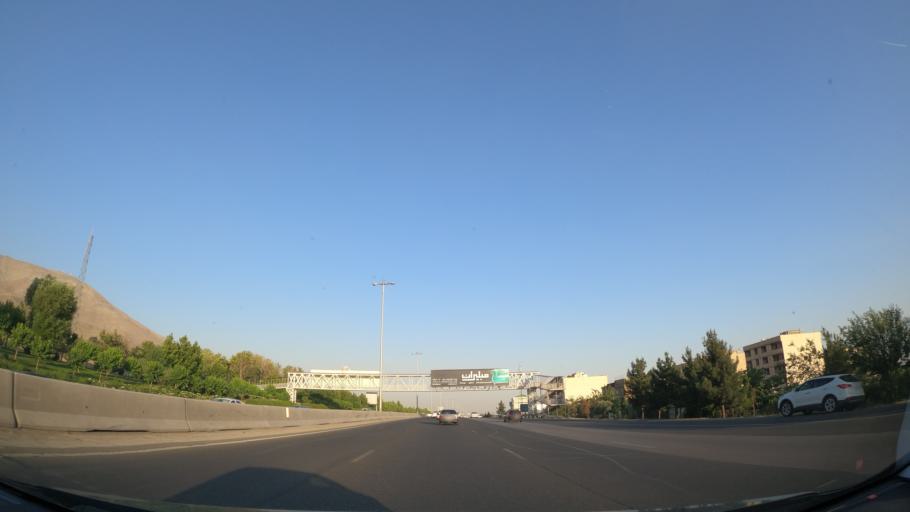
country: IR
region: Alborz
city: Karaj
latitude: 35.7832
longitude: 51.0301
